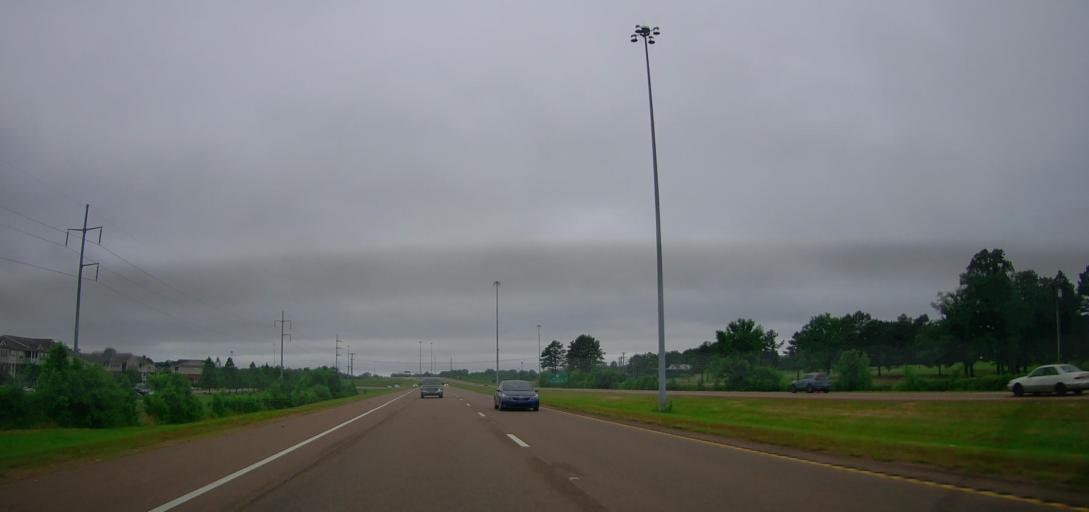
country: US
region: Mississippi
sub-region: De Soto County
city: Olive Branch
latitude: 34.9690
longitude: -89.8217
